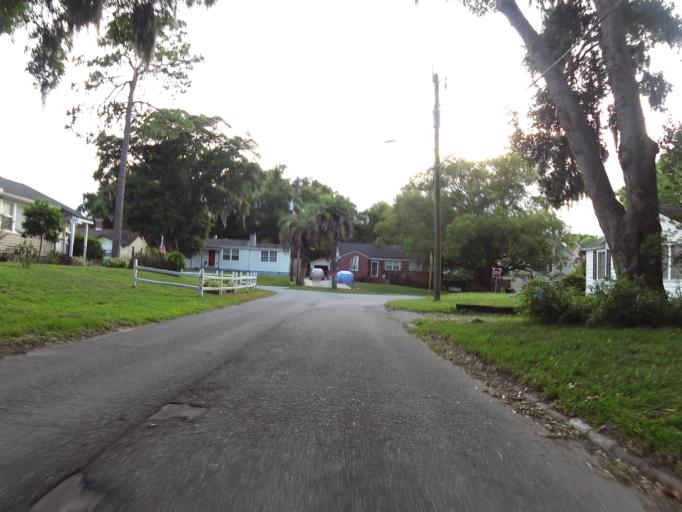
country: US
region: Florida
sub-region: Duval County
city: Jacksonville
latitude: 30.3041
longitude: -81.6258
